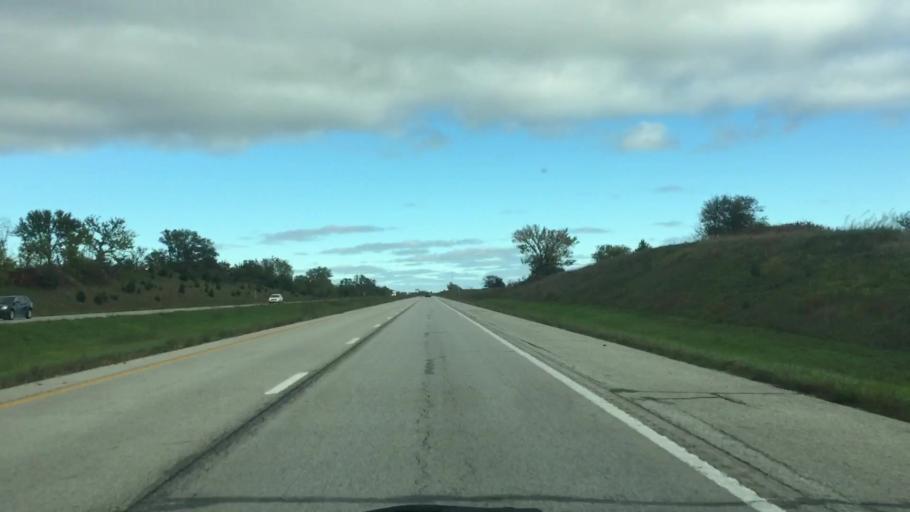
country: US
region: Missouri
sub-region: Harrison County
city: Bethany
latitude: 40.3272
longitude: -94.0114
